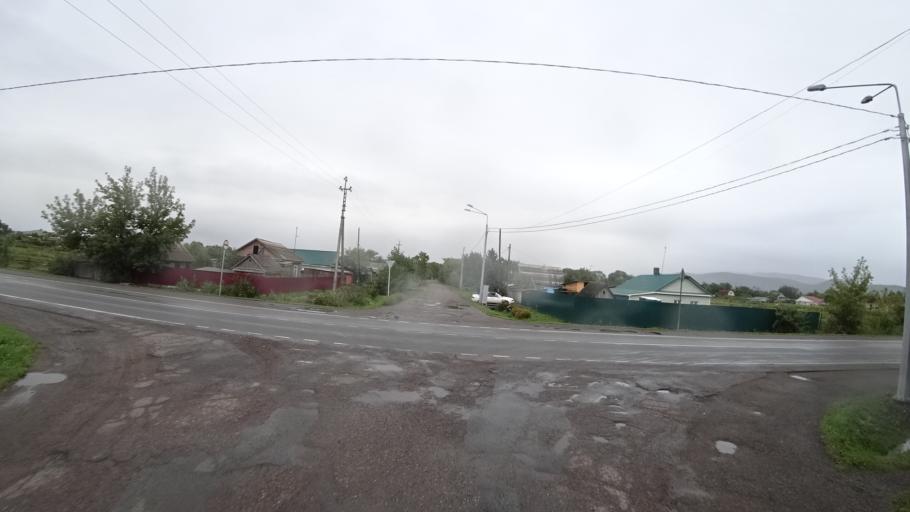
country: RU
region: Primorskiy
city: Chernigovka
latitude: 44.3345
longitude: 132.5805
